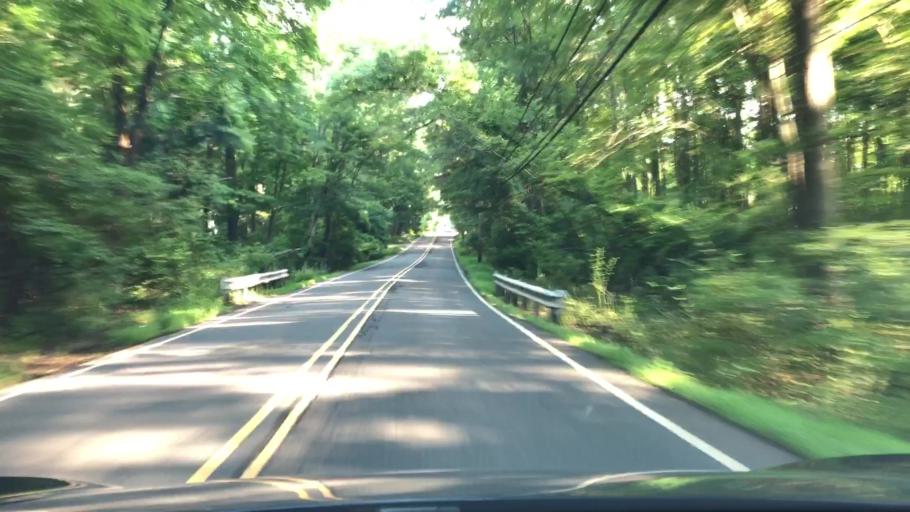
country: US
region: New Jersey
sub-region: Mercer County
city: Princeton
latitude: 40.3398
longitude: -74.7030
